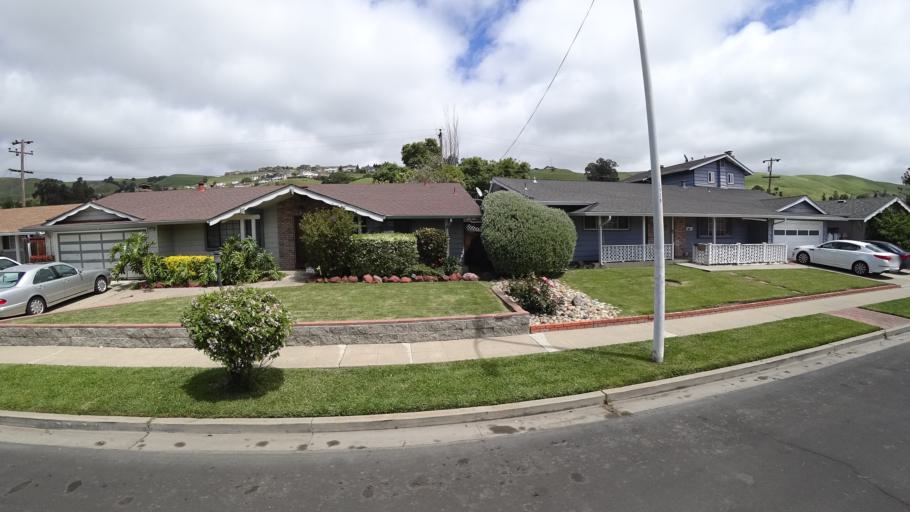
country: US
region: California
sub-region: Alameda County
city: Union City
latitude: 37.6236
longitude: -122.0389
